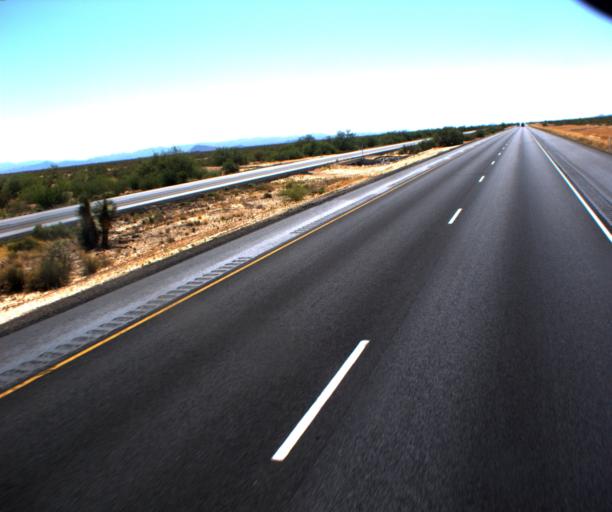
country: US
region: Arizona
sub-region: Yavapai County
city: Congress
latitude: 34.0871
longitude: -112.8990
